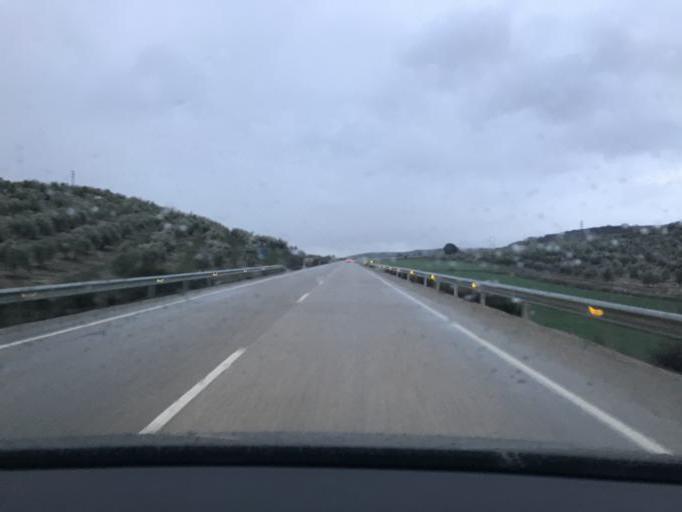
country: ES
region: Andalusia
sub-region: Provincia de Granada
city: Campotejar
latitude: 37.4693
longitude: -3.5830
